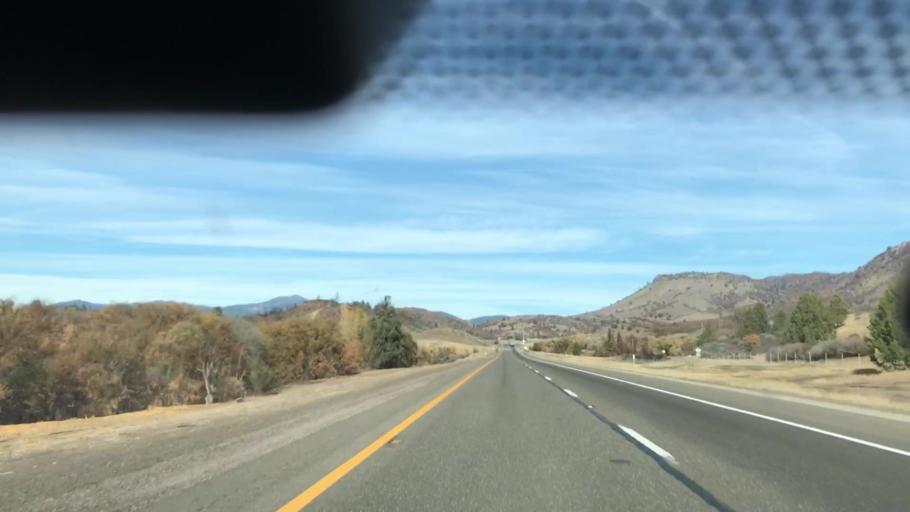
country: US
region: California
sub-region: Siskiyou County
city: Yreka
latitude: 41.9419
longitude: -122.5848
